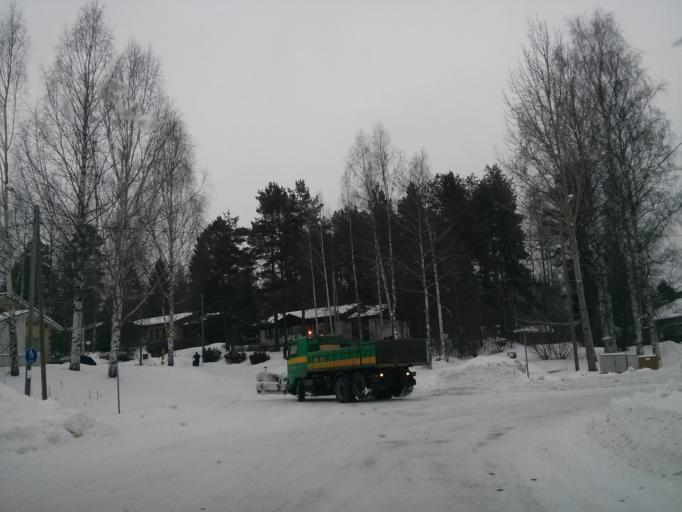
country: FI
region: Southern Savonia
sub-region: Savonlinna
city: Savonlinna
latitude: 61.8876
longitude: 28.8077
